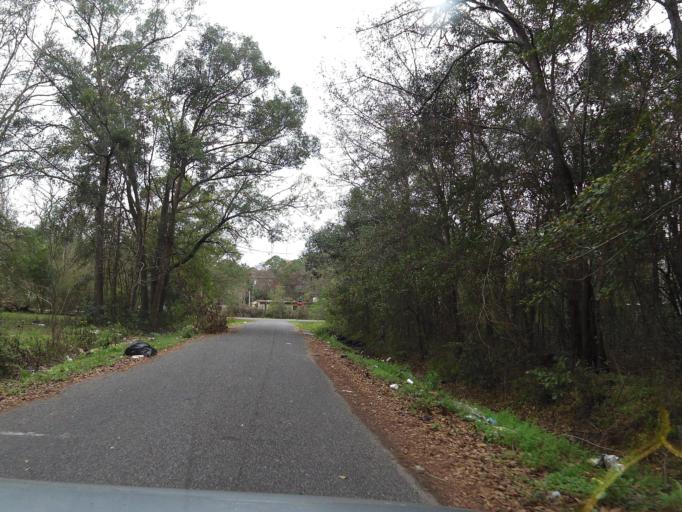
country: US
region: Florida
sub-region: Duval County
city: Jacksonville
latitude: 30.3749
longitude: -81.7006
